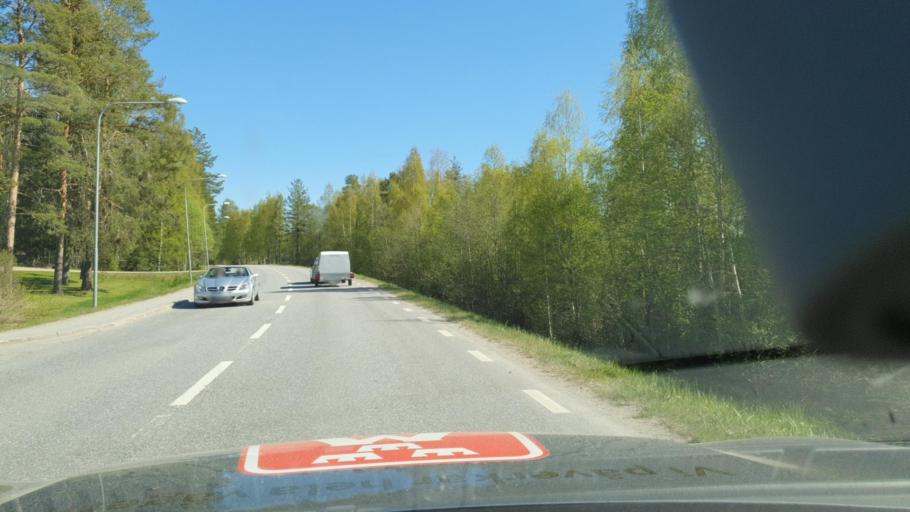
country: SE
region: Vaesternorrland
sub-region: OErnskoeldsviks Kommun
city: Ornskoldsvik
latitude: 63.5527
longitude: 18.5890
